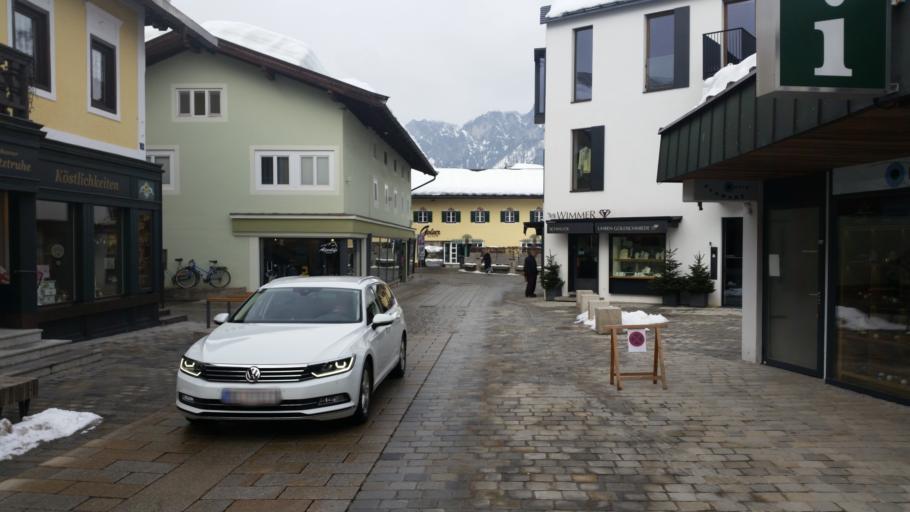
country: AT
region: Tyrol
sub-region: Politischer Bezirk Kitzbuhel
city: Sankt Johann in Tirol
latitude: 47.5218
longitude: 12.4270
